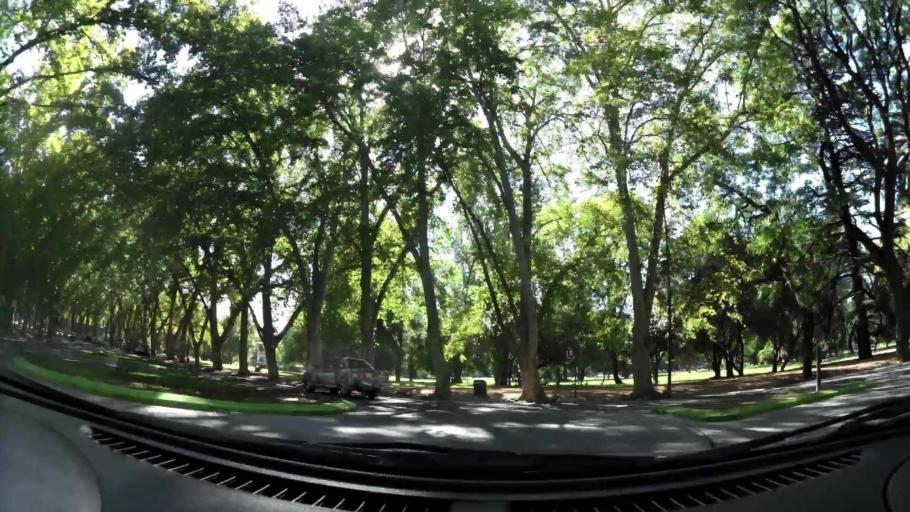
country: AR
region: Mendoza
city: Mendoza
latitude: -32.8881
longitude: -68.8635
